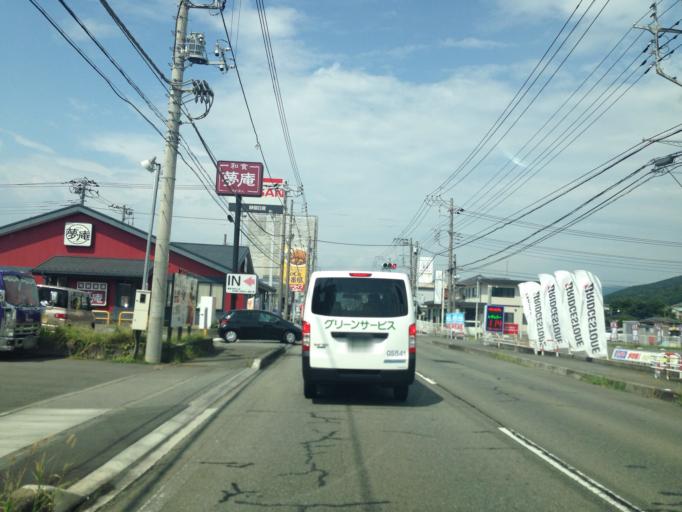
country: JP
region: Shizuoka
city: Mishima
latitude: 35.0020
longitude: 138.9399
